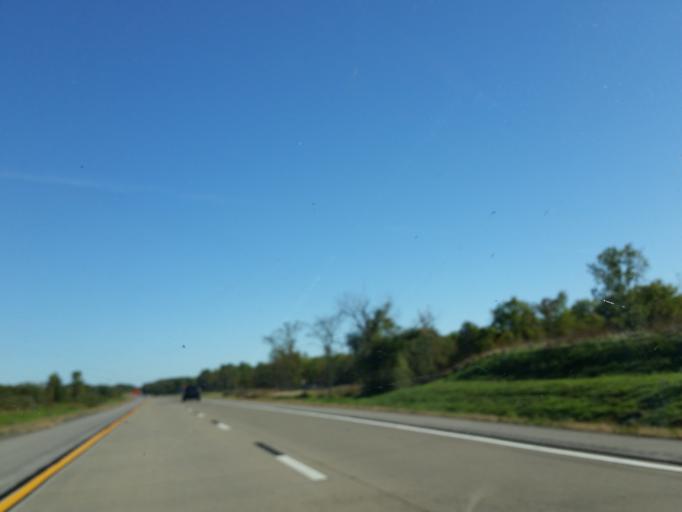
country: US
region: New York
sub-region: Erie County
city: Eden
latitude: 42.6746
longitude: -78.9464
